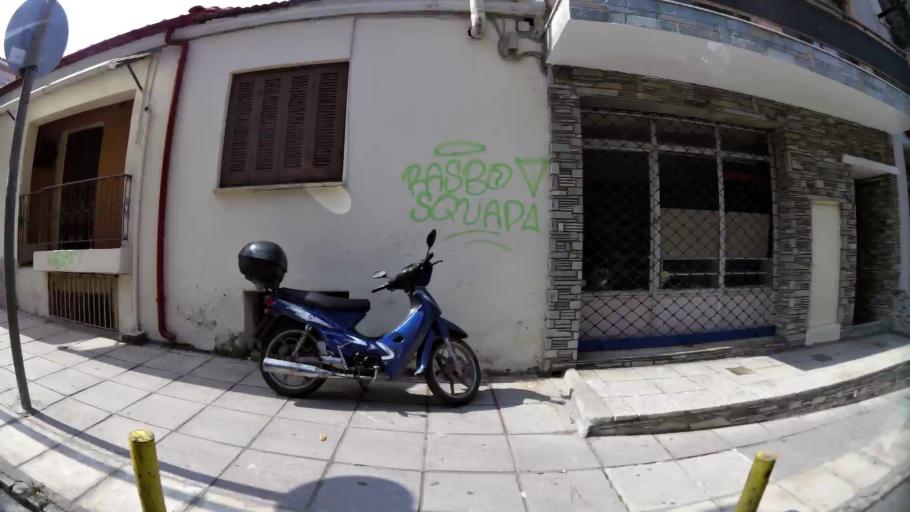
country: GR
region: Central Macedonia
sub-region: Nomos Thessalonikis
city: Agios Pavlos
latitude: 40.6422
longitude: 22.9583
